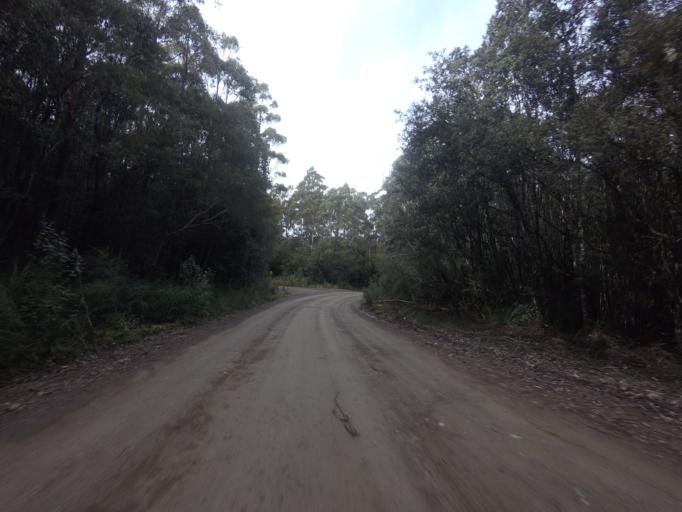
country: AU
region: Tasmania
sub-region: Huon Valley
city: Geeveston
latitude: -43.5041
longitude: 146.8770
